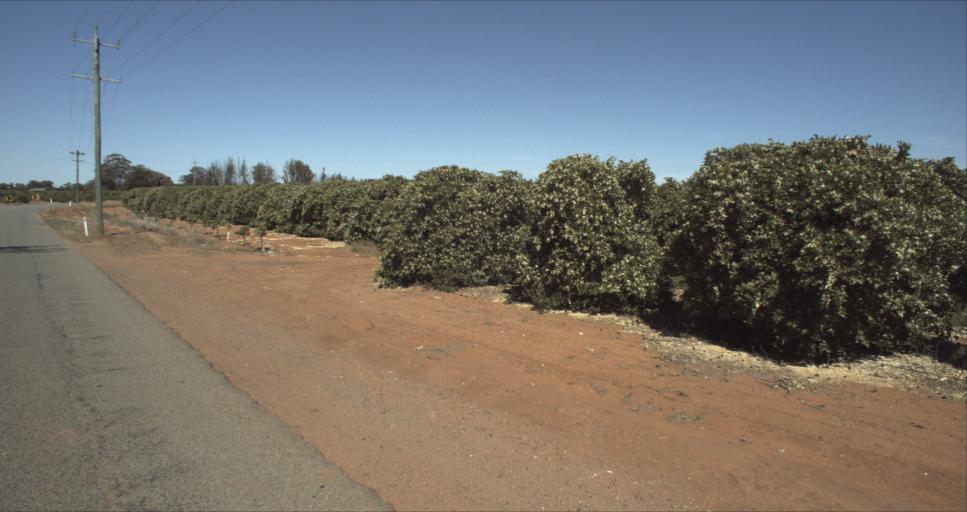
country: AU
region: New South Wales
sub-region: Leeton
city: Leeton
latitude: -34.5337
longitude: 146.3542
